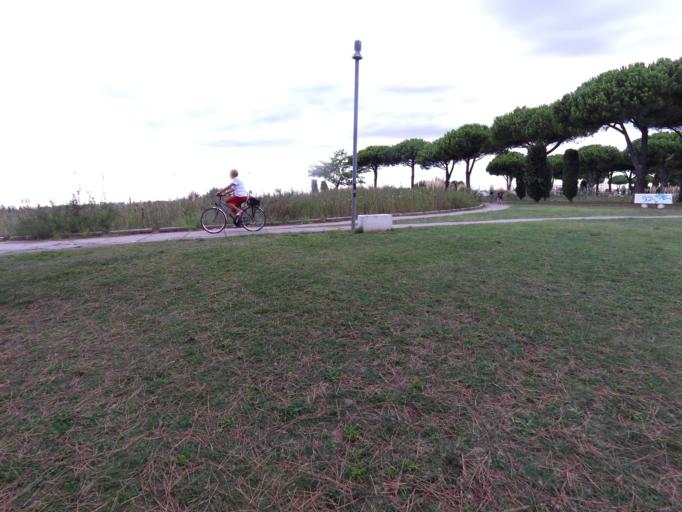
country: FR
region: Languedoc-Roussillon
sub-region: Departement du Gard
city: Le Grau-du-Roi
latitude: 43.5285
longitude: 4.1409
